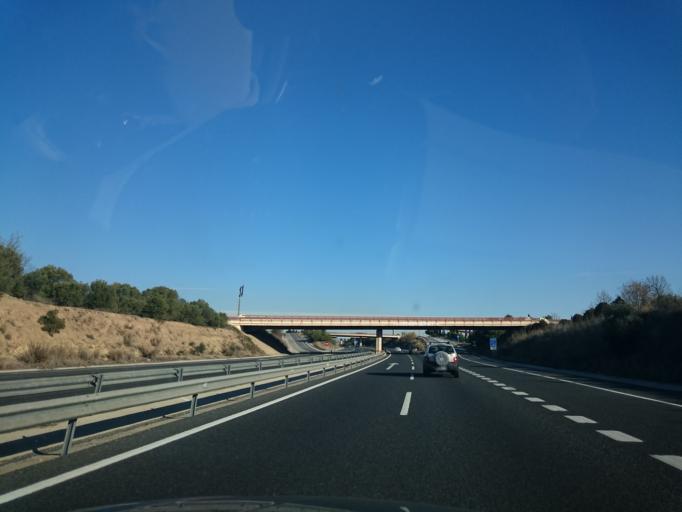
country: ES
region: Catalonia
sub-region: Provincia de Tarragona
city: Vila-seca
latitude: 41.1022
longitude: 1.1529
